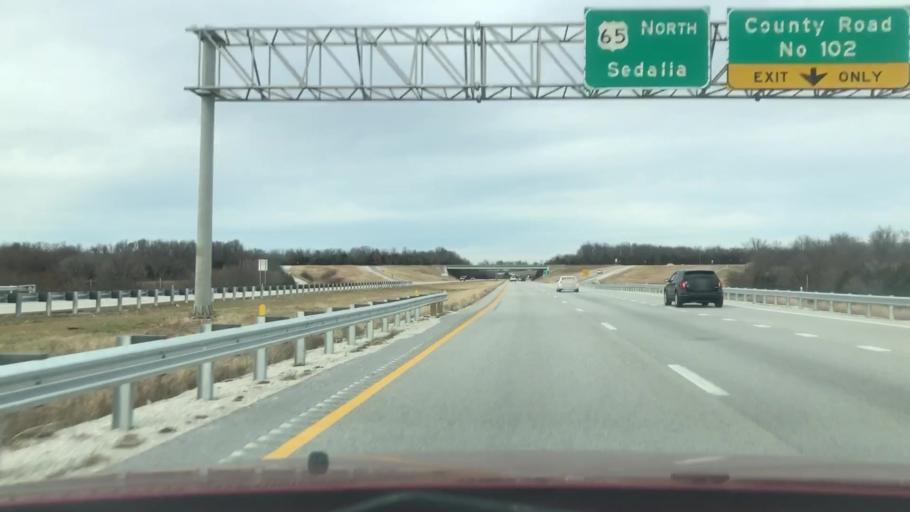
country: US
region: Missouri
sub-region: Greene County
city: Springfield
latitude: 37.2554
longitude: -93.2243
